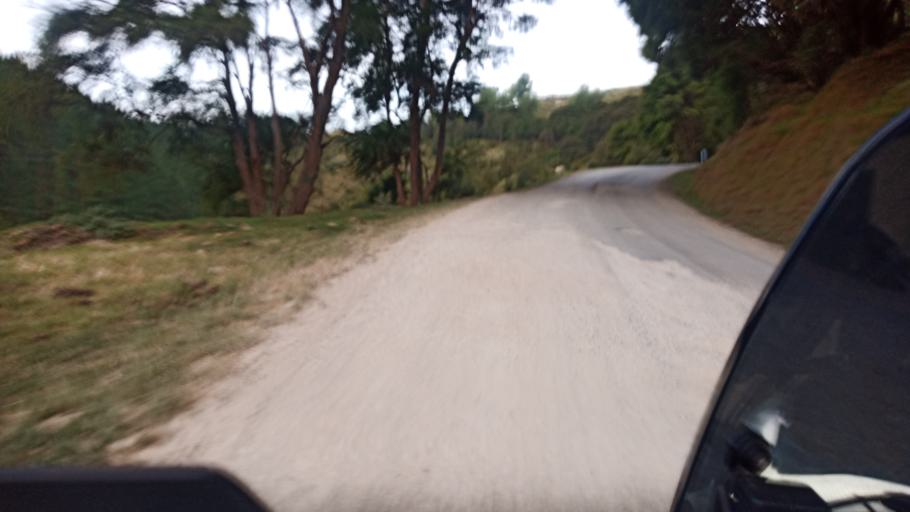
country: NZ
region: Gisborne
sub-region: Gisborne District
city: Gisborne
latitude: -38.4800
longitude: 177.9687
